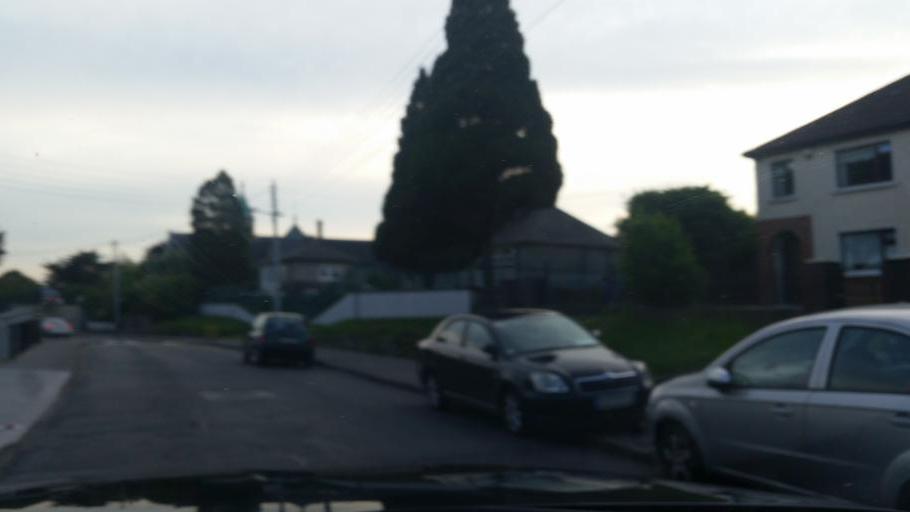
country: IE
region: Leinster
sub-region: Dublin City
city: Finglas
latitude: 53.3891
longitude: -6.2949
